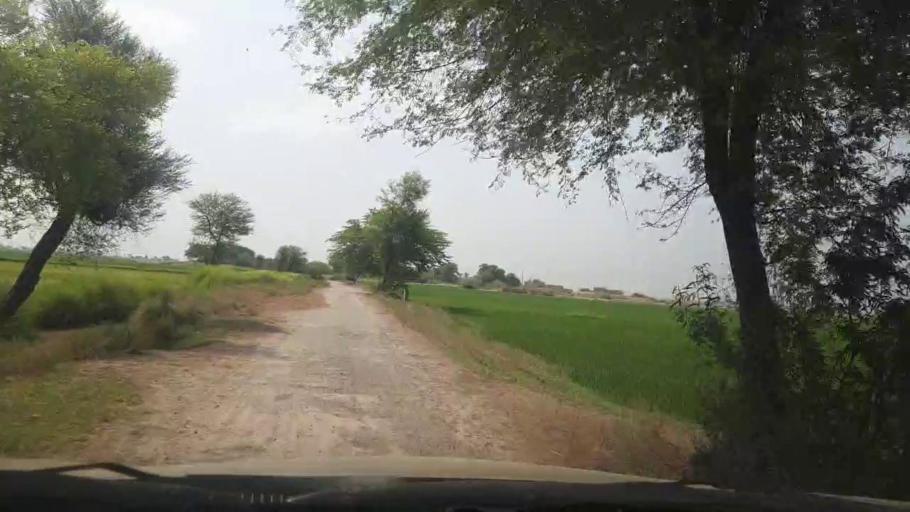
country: PK
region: Sindh
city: Larkana
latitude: 27.6832
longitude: 68.2021
